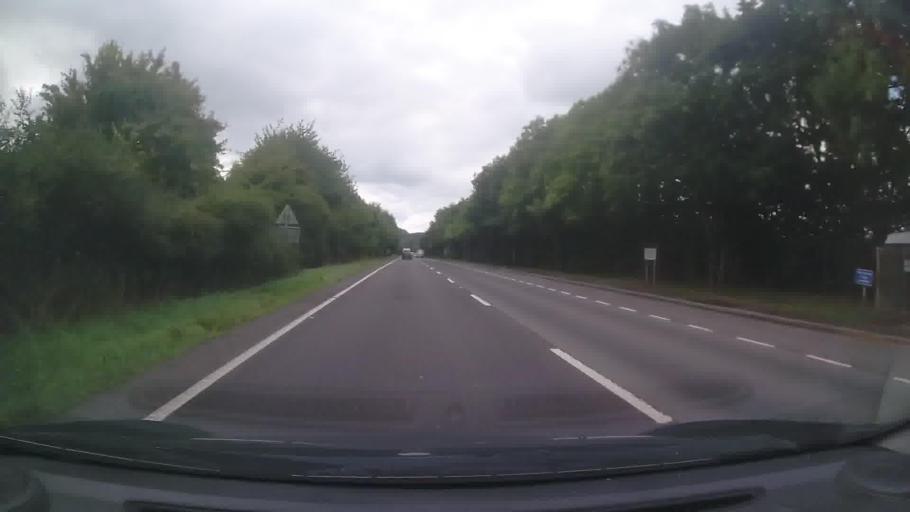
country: GB
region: England
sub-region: Shropshire
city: Oswestry
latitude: 52.8373
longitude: -3.0470
